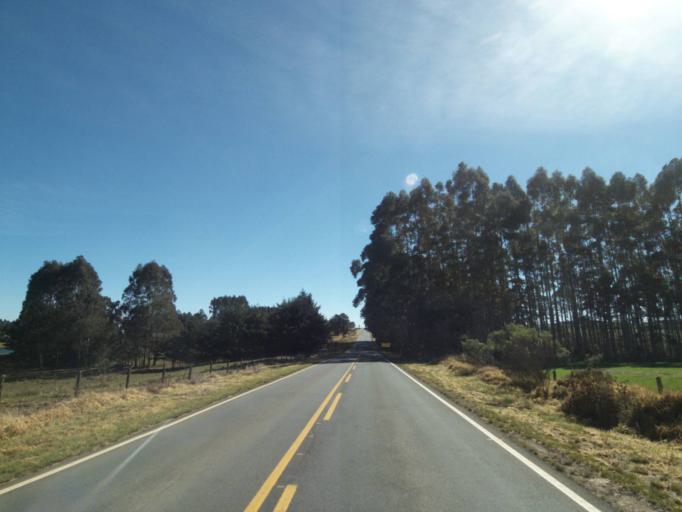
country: BR
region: Parana
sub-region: Castro
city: Castro
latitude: -24.7168
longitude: -50.1900
